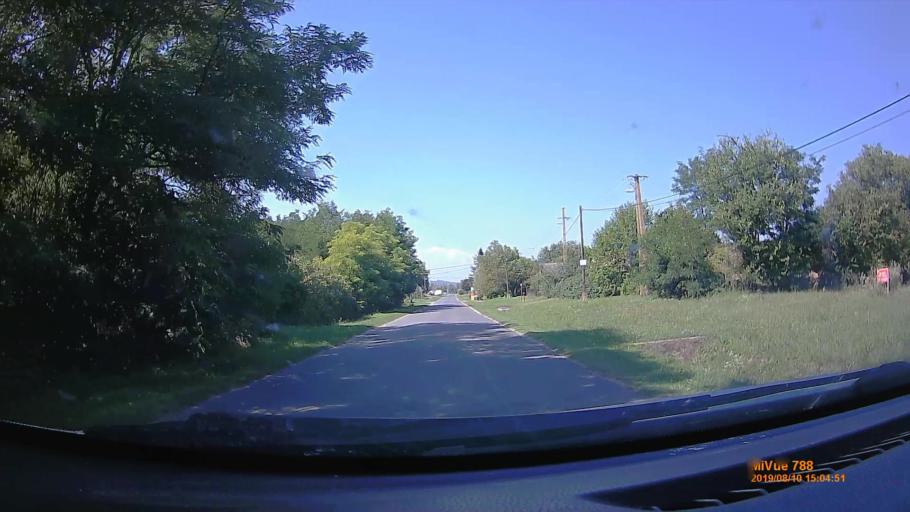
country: HU
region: Somogy
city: Lengyeltoti
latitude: 46.6771
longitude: 17.5658
